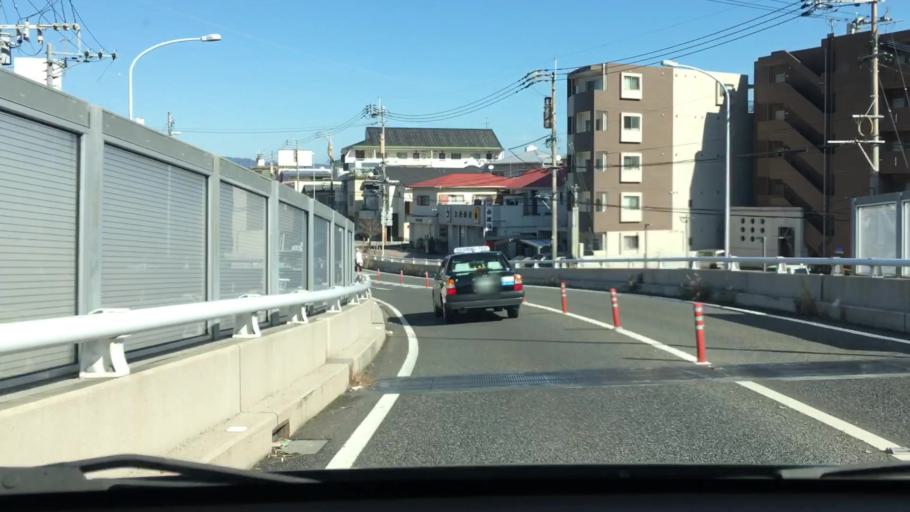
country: JP
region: Kagoshima
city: Kagoshima-shi
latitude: 31.5632
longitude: 130.5447
